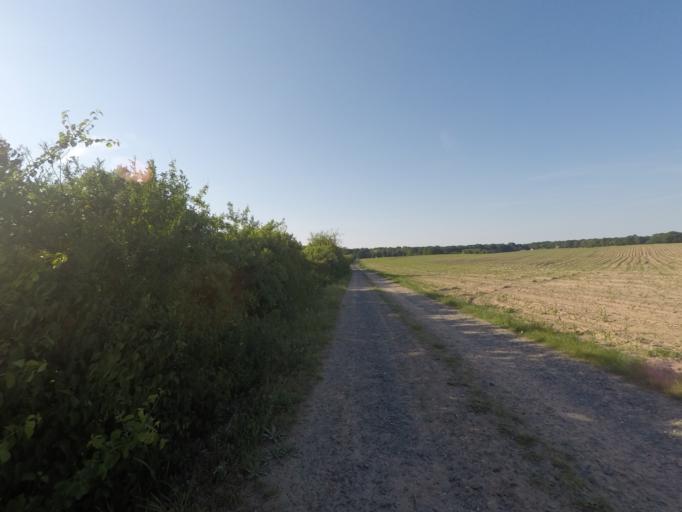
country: DE
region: Brandenburg
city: Joachimsthal
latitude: 52.8988
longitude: 13.7038
